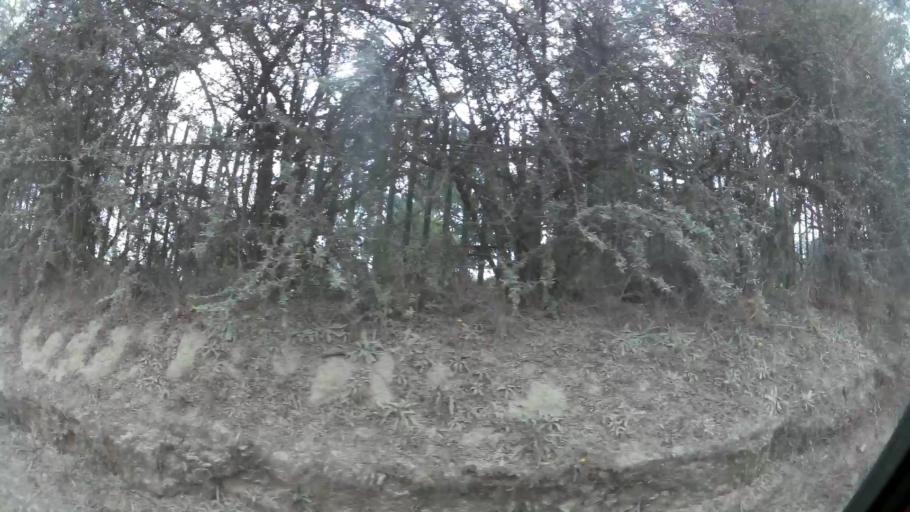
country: ZA
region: Gauteng
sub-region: West Rand District Municipality
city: Muldersdriseloop
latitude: -26.0683
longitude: 27.8870
